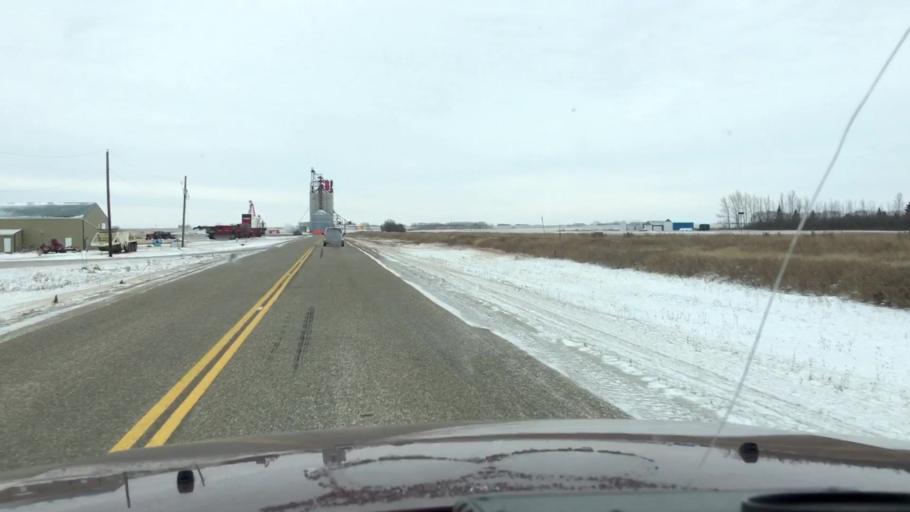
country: CA
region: Saskatchewan
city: Watrous
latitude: 51.2526
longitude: -105.9807
